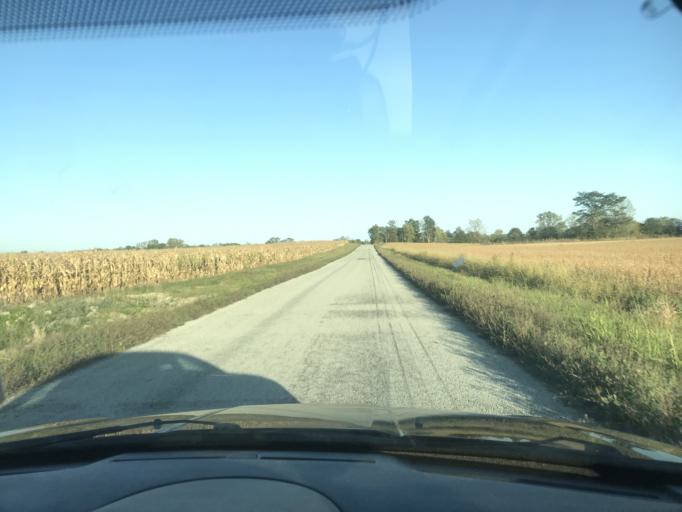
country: US
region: Ohio
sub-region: Logan County
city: West Liberty
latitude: 40.2334
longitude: -83.8317
